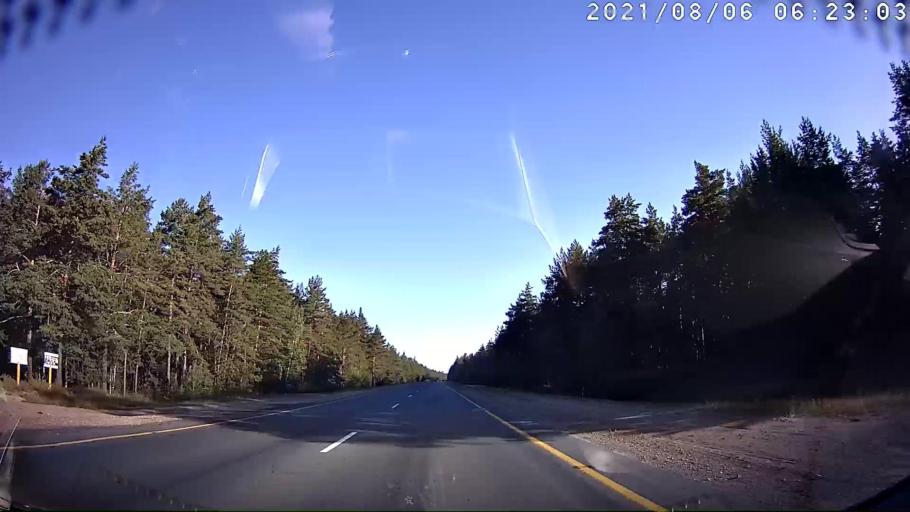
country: RU
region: Mariy-El
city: Krasnogorskiy
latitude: 56.0898
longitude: 48.3499
